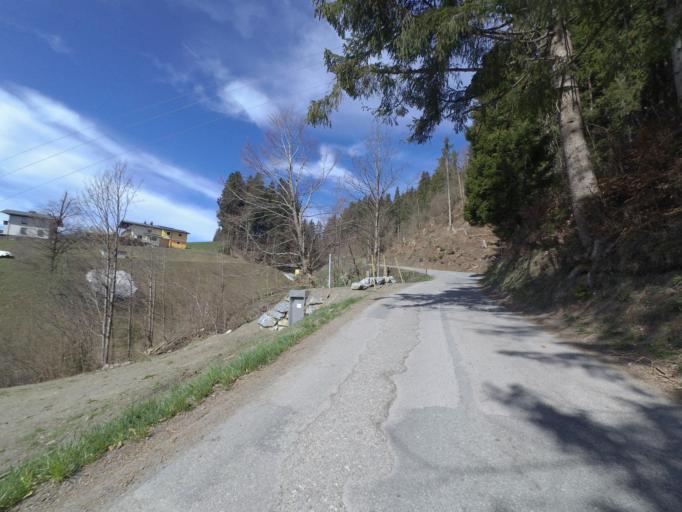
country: AT
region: Salzburg
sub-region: Politischer Bezirk Sankt Johann im Pongau
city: Sankt Veit im Pongau
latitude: 47.3346
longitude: 13.1431
